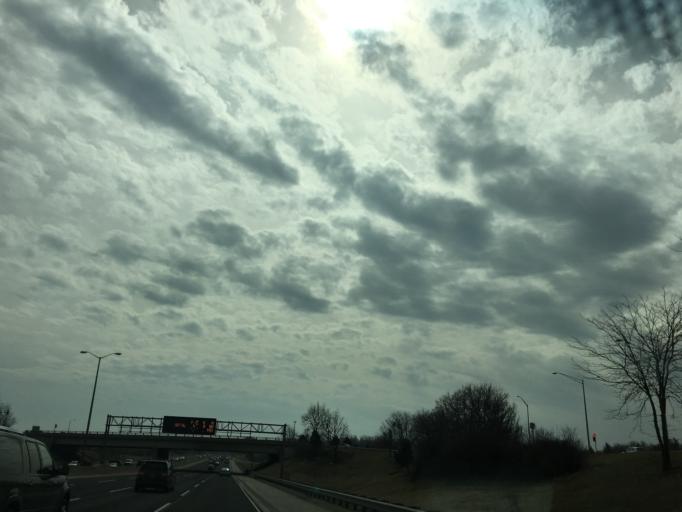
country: US
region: Illinois
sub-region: DuPage County
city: Woodridge
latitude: 41.7734
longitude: -88.0471
